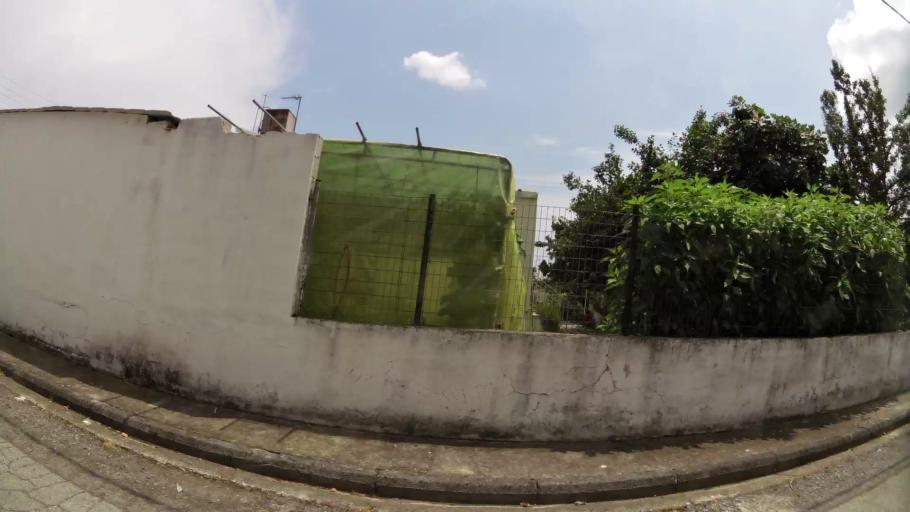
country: GR
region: Central Macedonia
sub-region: Nomos Pierias
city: Peristasi
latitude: 40.2768
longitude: 22.5430
